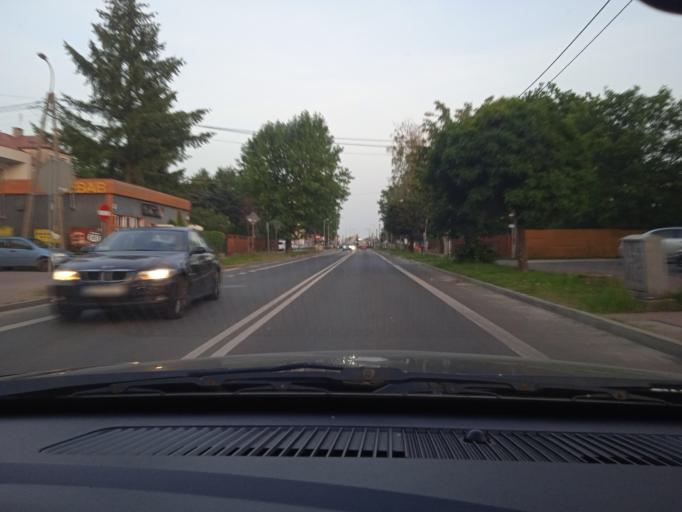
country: PL
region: Masovian Voivodeship
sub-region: Powiat nowodworski
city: Nowy Dwor Mazowiecki
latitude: 52.4290
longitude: 20.7178
